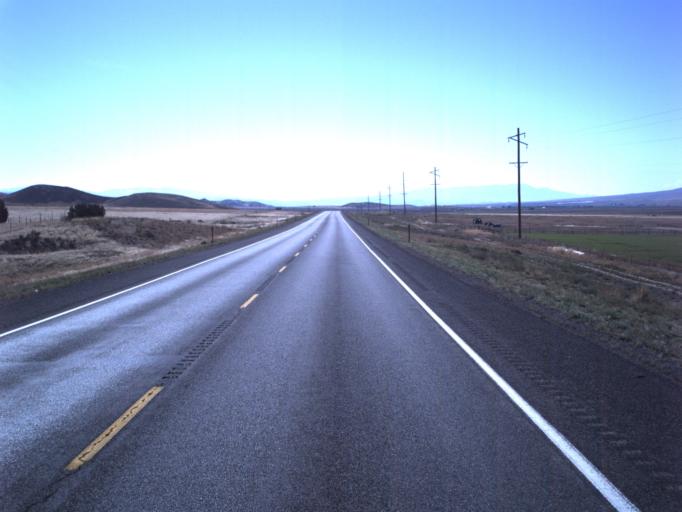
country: US
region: Utah
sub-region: Sanpete County
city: Gunnison
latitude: 39.2209
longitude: -111.8482
